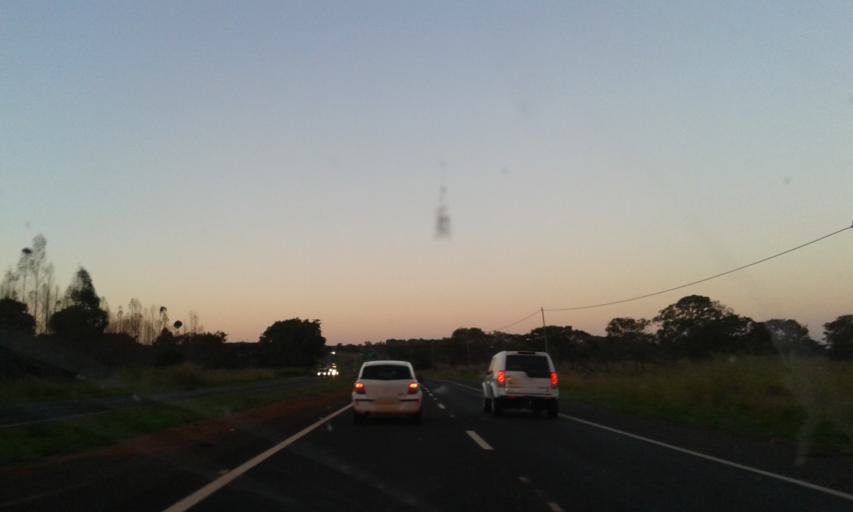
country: BR
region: Minas Gerais
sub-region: Monte Alegre De Minas
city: Monte Alegre de Minas
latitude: -18.8812
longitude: -48.6071
